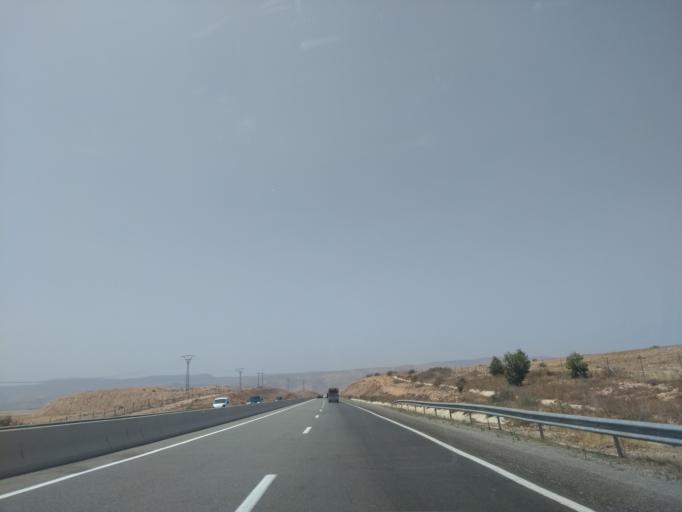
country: MA
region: Marrakech-Tensift-Al Haouz
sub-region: Chichaoua
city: Taouloukoult
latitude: 31.2389
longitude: -8.8944
